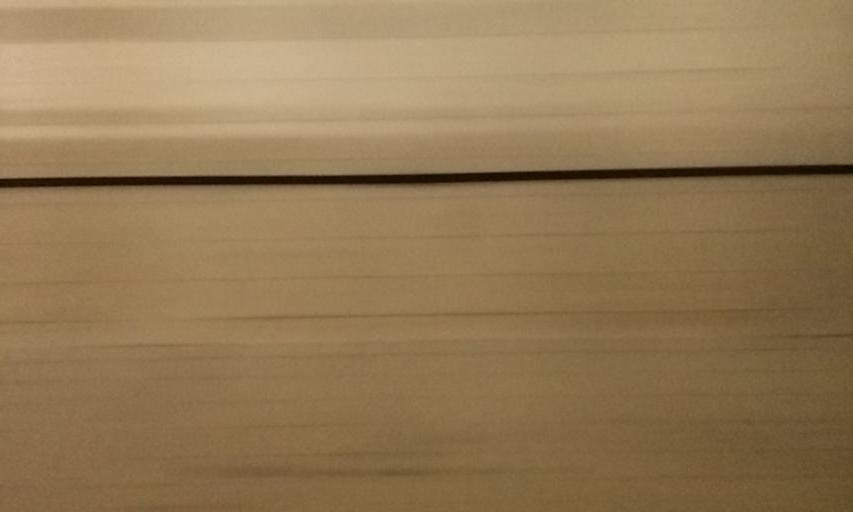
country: JP
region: Tokyo
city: Hino
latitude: 35.6440
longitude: 139.4043
